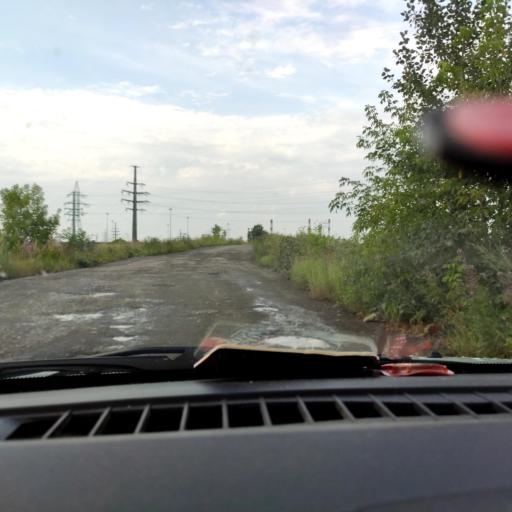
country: RU
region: Perm
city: Kondratovo
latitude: 57.9411
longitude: 56.1608
